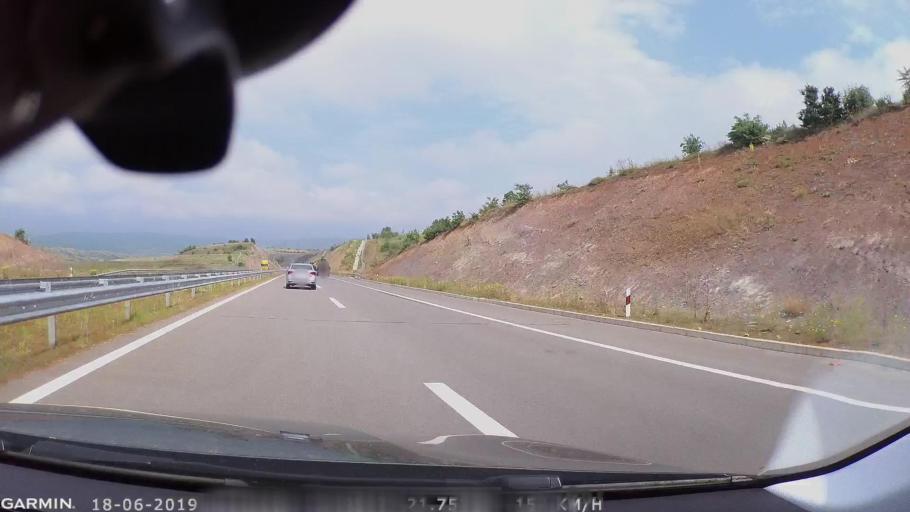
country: MK
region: Sveti Nikole
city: Gorobinci
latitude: 41.9247
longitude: 21.8400
